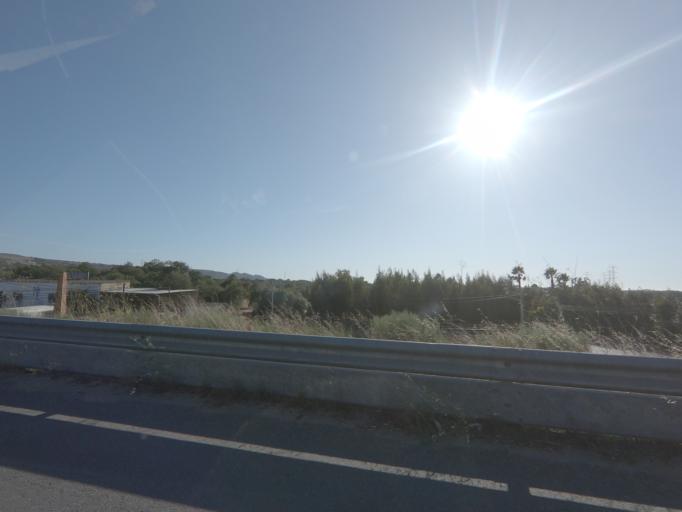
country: PT
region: Setubal
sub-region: Palmela
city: Palmela
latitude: 38.5847
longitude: -8.9162
